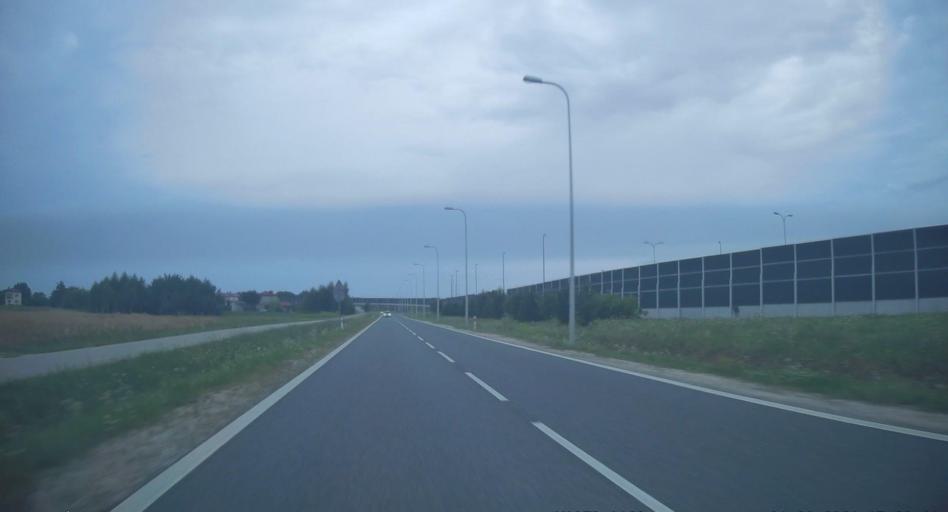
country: PL
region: Lesser Poland Voivodeship
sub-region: Powiat tarnowski
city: Wierzchoslawice
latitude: 50.0119
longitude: 20.8752
